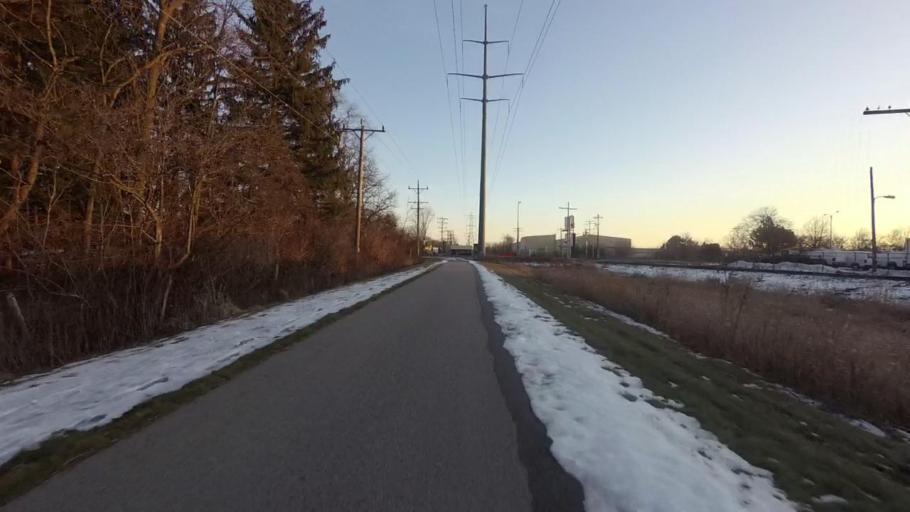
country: US
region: Wisconsin
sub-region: Milwaukee County
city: Brown Deer
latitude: 43.1494
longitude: -87.9549
